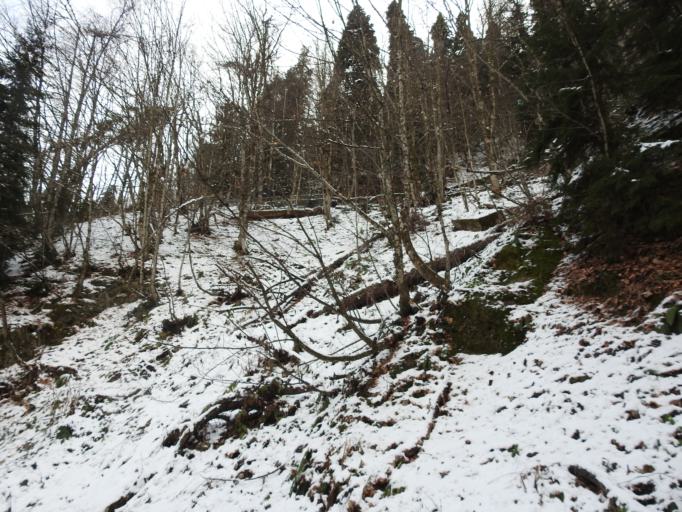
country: GE
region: Abkhazia
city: Gagra
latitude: 43.4786
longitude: 40.5524
